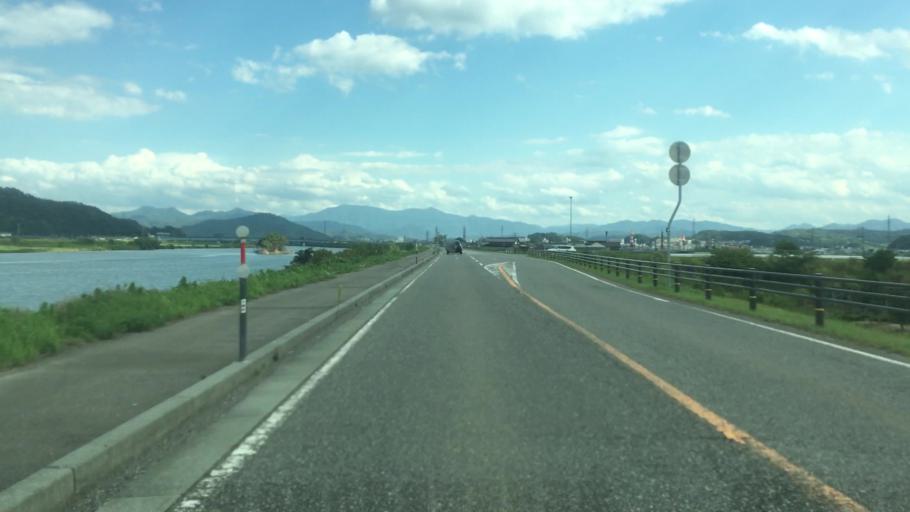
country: JP
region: Hyogo
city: Toyooka
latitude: 35.5692
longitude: 134.8093
